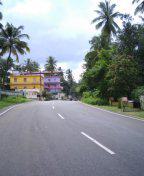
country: IN
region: Kerala
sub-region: Thrissur District
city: Trichur
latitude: 10.5278
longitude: 76.3593
